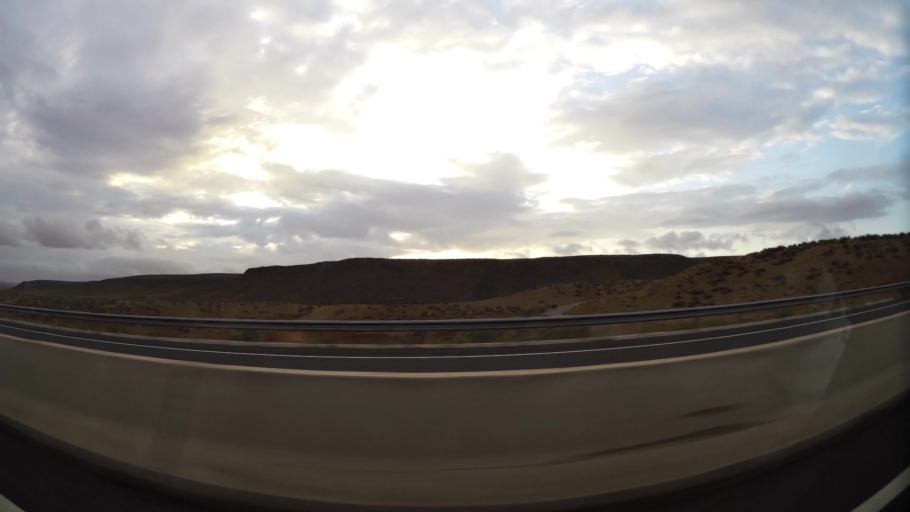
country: MA
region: Oriental
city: Taourirt
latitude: 34.4512
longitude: -3.0499
